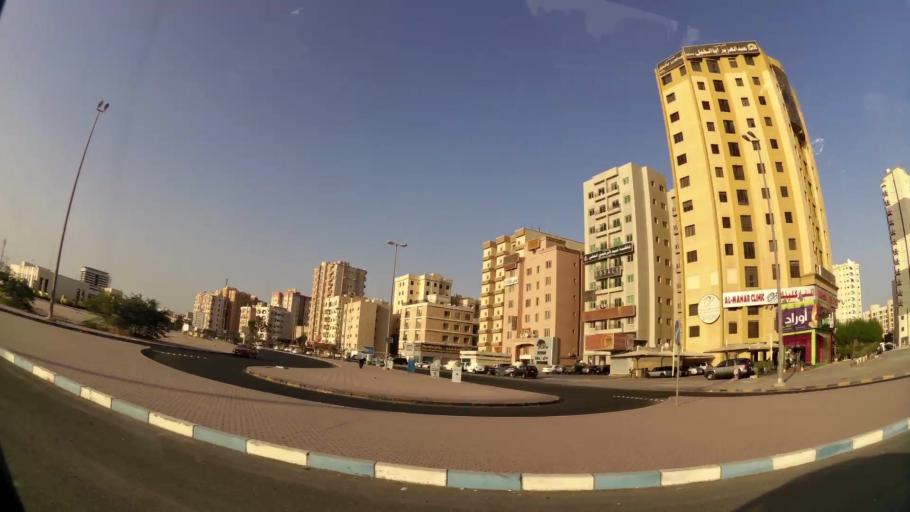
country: KW
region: Muhafazat Hawalli
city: As Salimiyah
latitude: 29.3246
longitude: 48.0850
